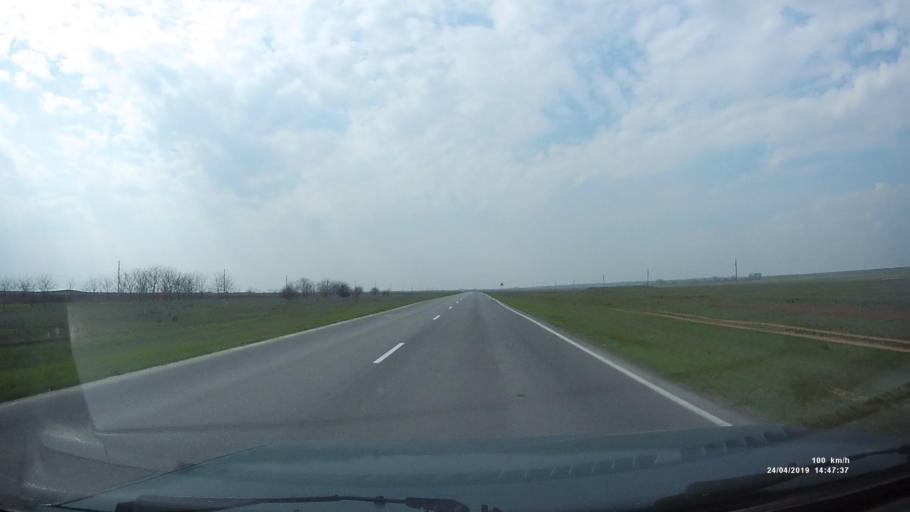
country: RU
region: Rostov
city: Remontnoye
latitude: 46.4932
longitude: 43.7699
